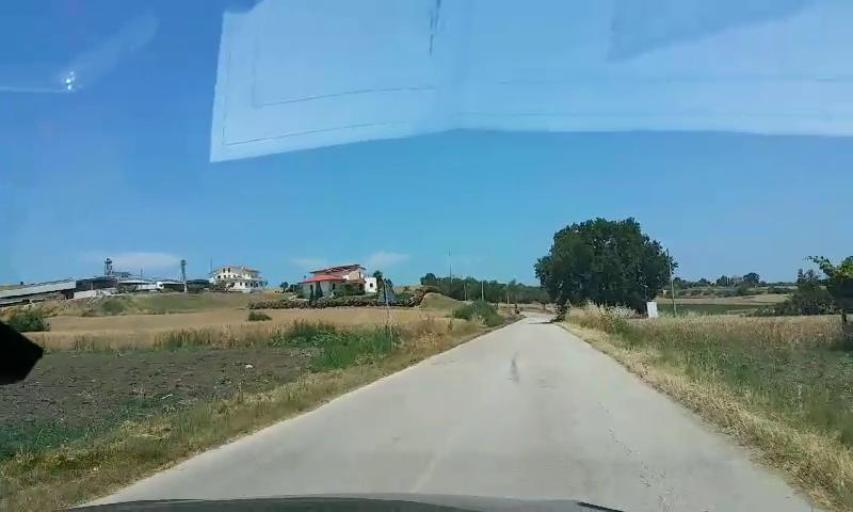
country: IT
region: Molise
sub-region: Provincia di Campobasso
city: San Giacomo degli Schiavoni
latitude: 41.9751
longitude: 14.9059
